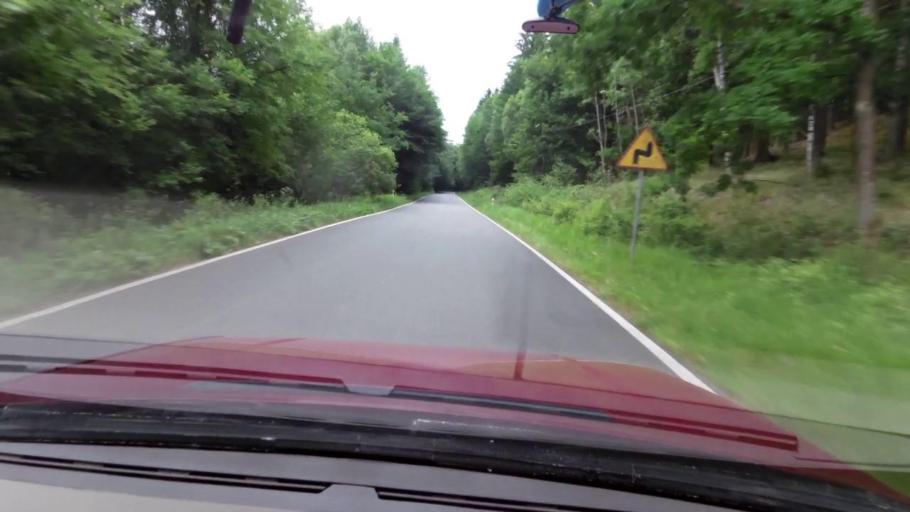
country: PL
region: West Pomeranian Voivodeship
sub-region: Powiat koszalinski
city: Polanow
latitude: 54.1567
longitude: 16.7044
